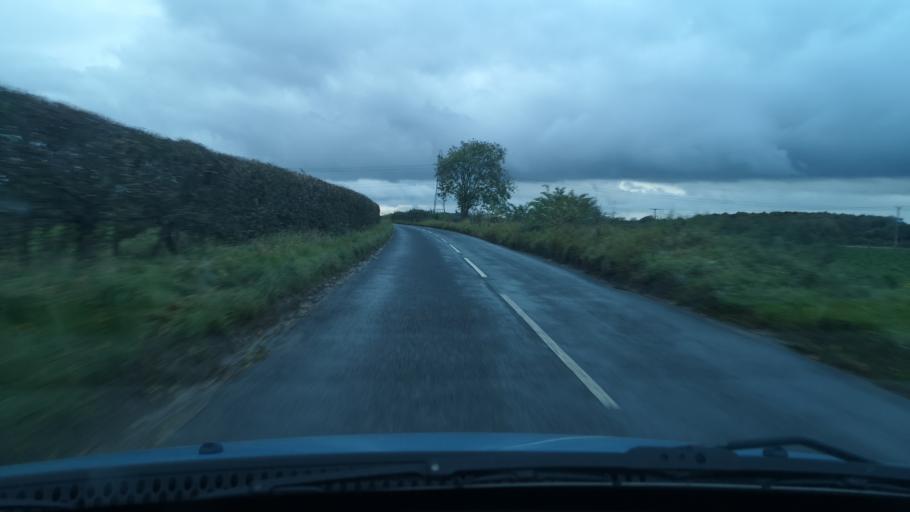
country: GB
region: England
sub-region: Doncaster
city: Norton
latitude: 53.6448
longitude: -1.2279
